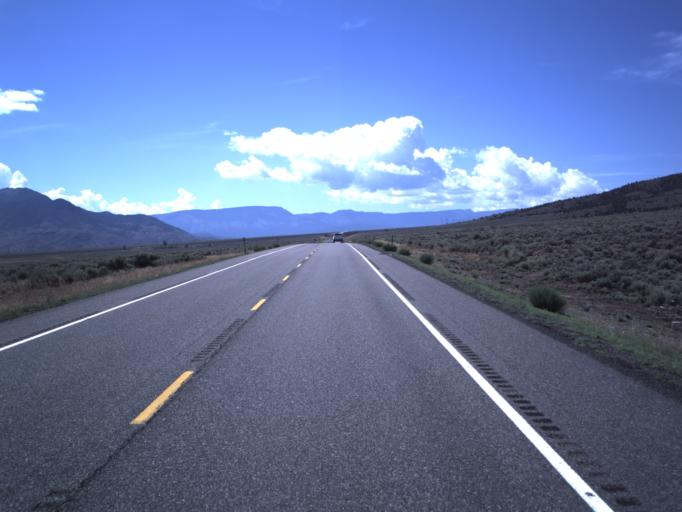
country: US
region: Utah
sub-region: Piute County
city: Junction
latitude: 38.3601
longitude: -112.2227
